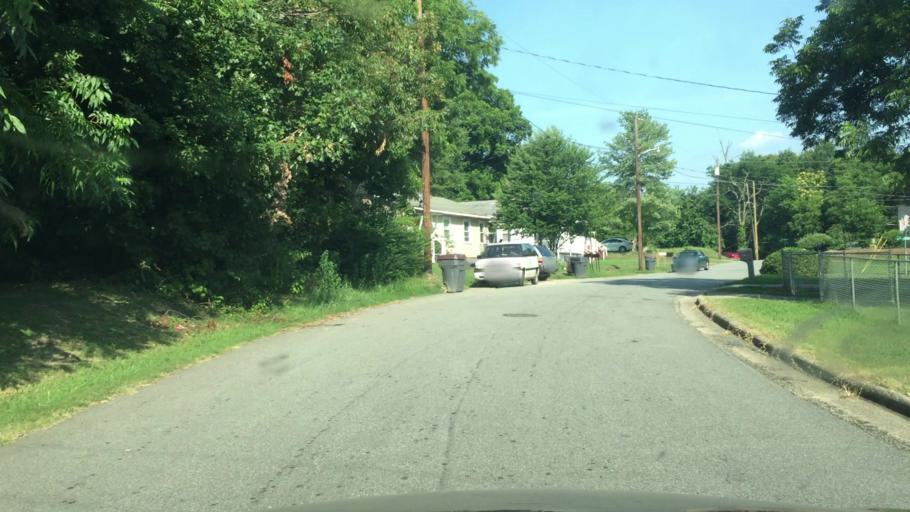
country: US
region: North Carolina
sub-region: Rockingham County
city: Reidsville
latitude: 36.3701
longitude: -79.6696
